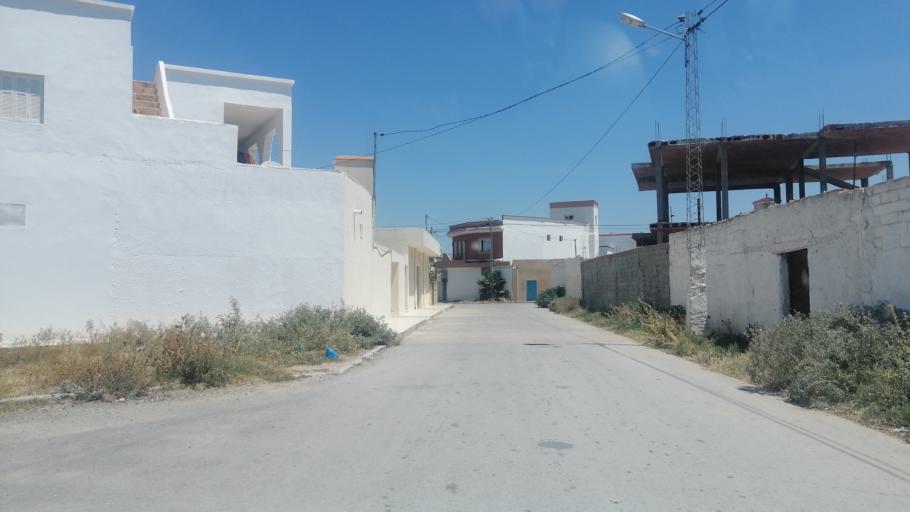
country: TN
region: Al Qayrawan
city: Sbikha
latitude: 36.1247
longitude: 10.0908
